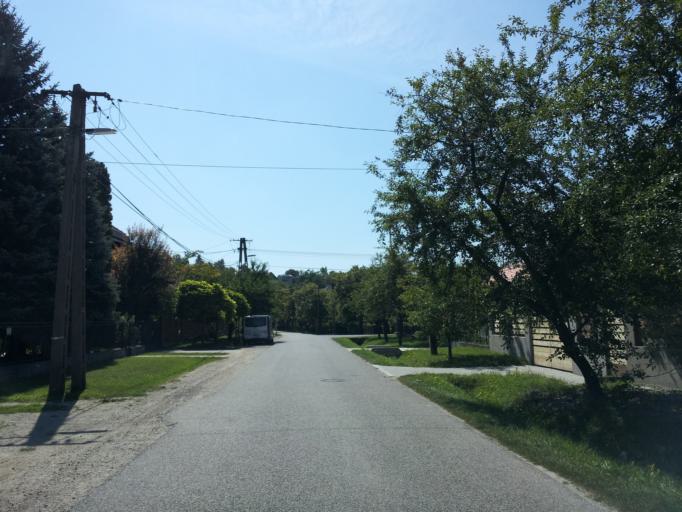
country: HU
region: Somogy
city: Zamardi
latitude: 46.8806
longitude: 17.9400
